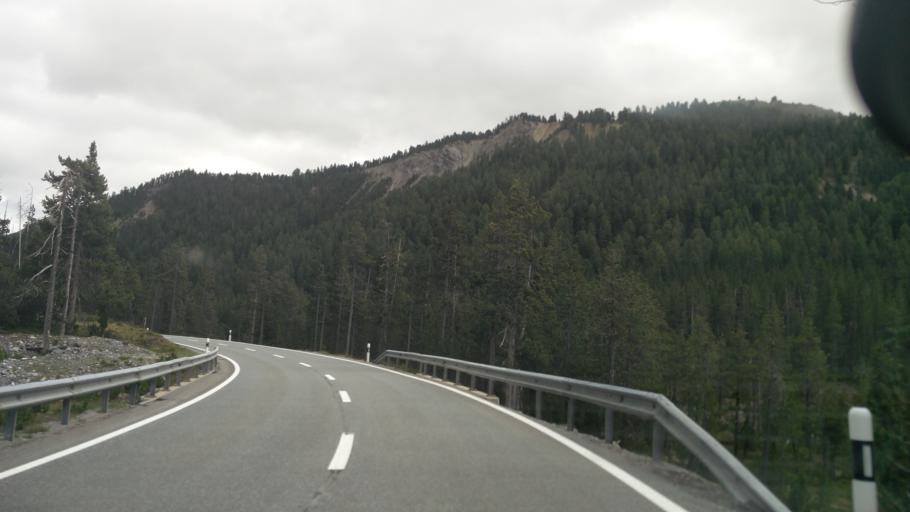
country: CH
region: Grisons
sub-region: Inn District
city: Scuol
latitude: 46.6545
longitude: 10.2492
